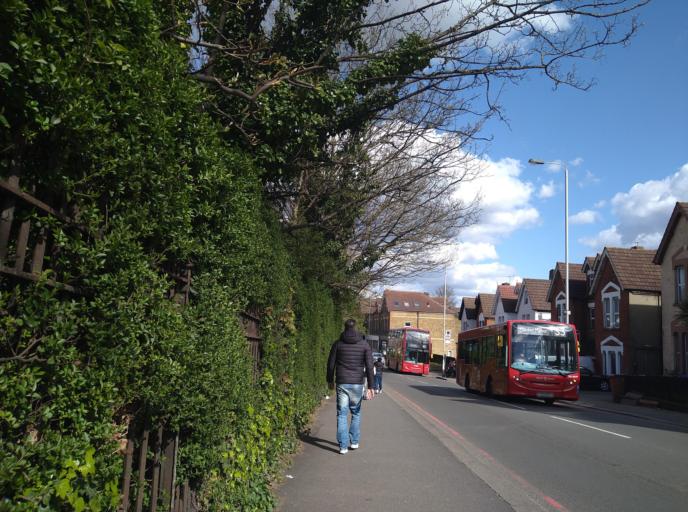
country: GB
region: England
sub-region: Greater London
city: Sutton
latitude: 51.3623
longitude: -0.1870
